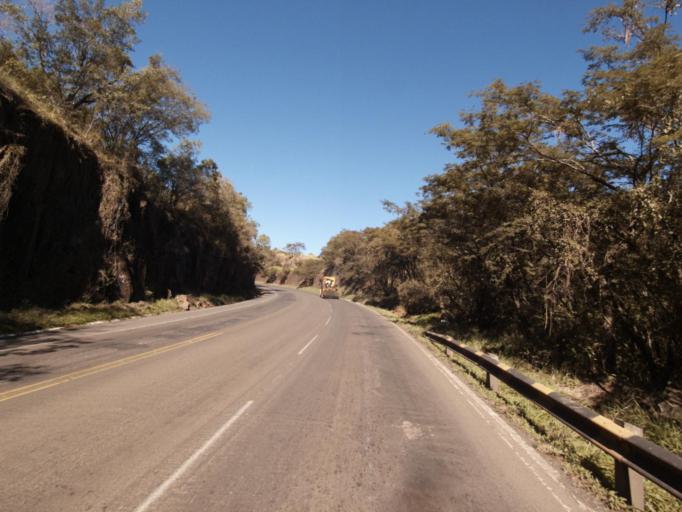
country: BR
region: Santa Catarina
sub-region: Chapeco
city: Chapeco
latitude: -26.9539
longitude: -52.7774
